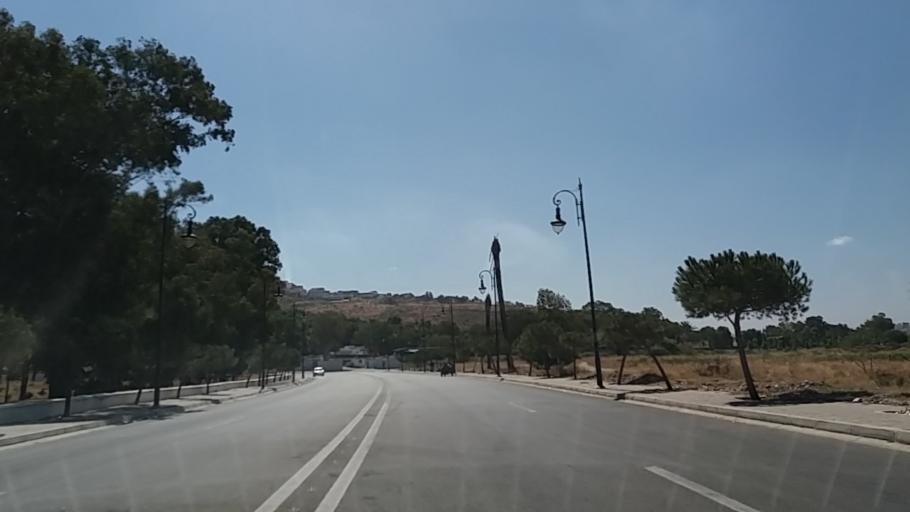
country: MA
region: Tanger-Tetouan
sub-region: Tanger-Assilah
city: Tangier
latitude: 35.7787
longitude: -5.7639
